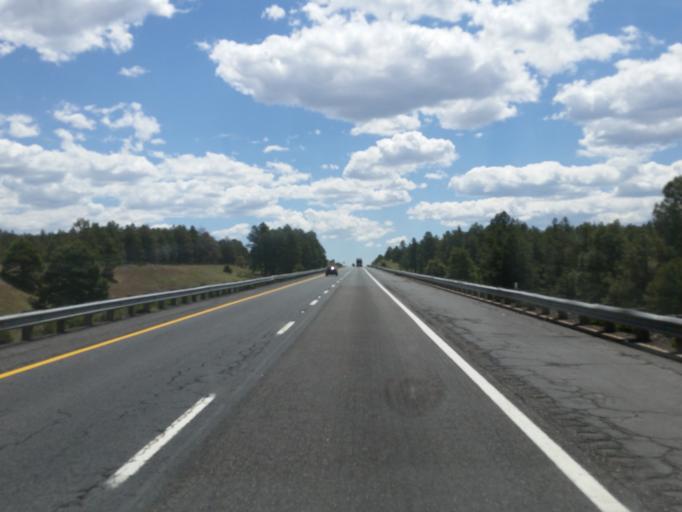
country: US
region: Arizona
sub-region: Coconino County
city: Parks
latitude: 35.2557
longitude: -112.0140
